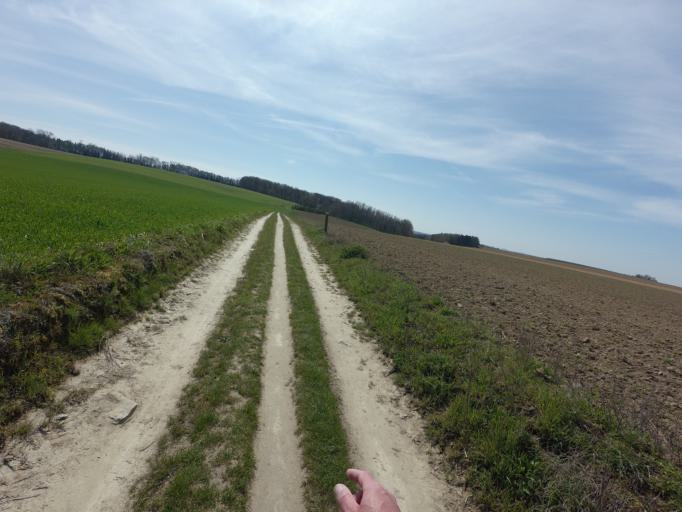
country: NL
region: Limburg
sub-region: Eijsden-Margraten
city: Eijsden
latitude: 50.7826
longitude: 5.7693
